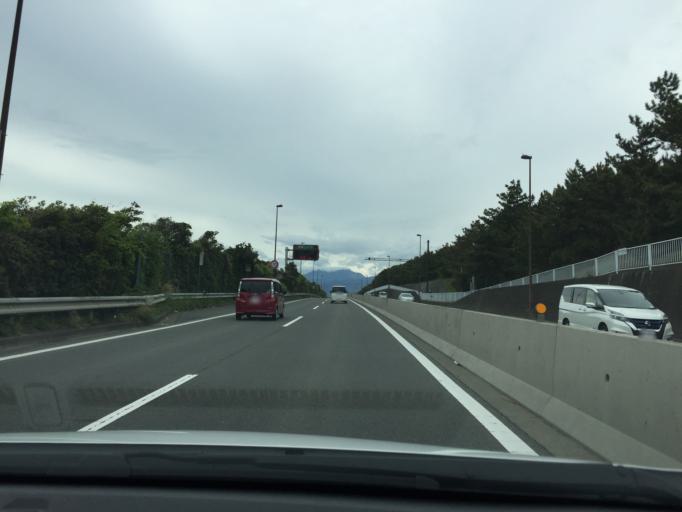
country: JP
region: Kanagawa
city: Oiso
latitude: 35.3047
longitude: 139.3017
